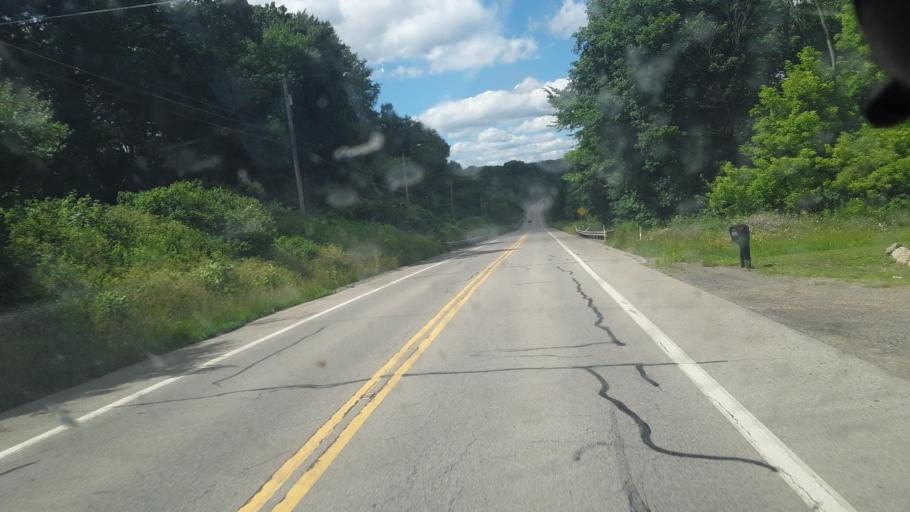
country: US
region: Pennsylvania
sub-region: Butler County
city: Slippery Rock
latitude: 40.9775
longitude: -80.1682
